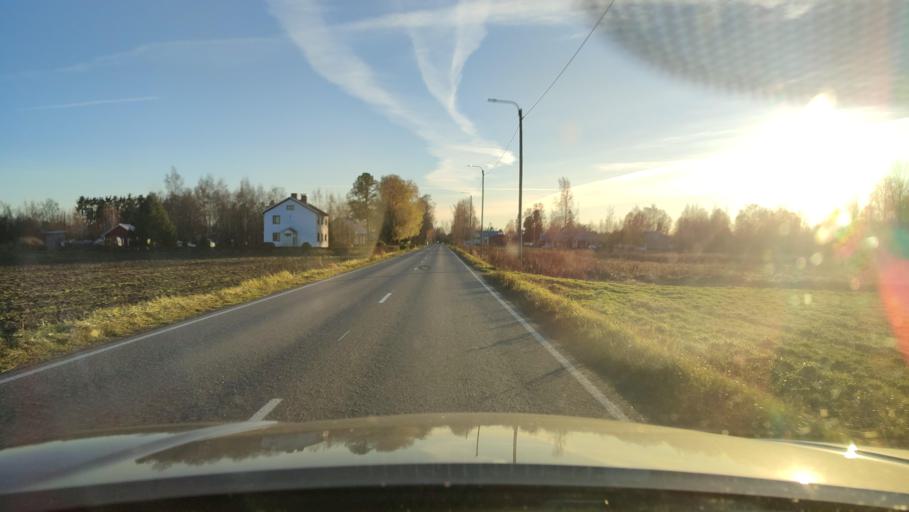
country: FI
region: Ostrobothnia
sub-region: Sydosterbotten
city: Naerpes
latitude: 62.6181
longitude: 21.4798
